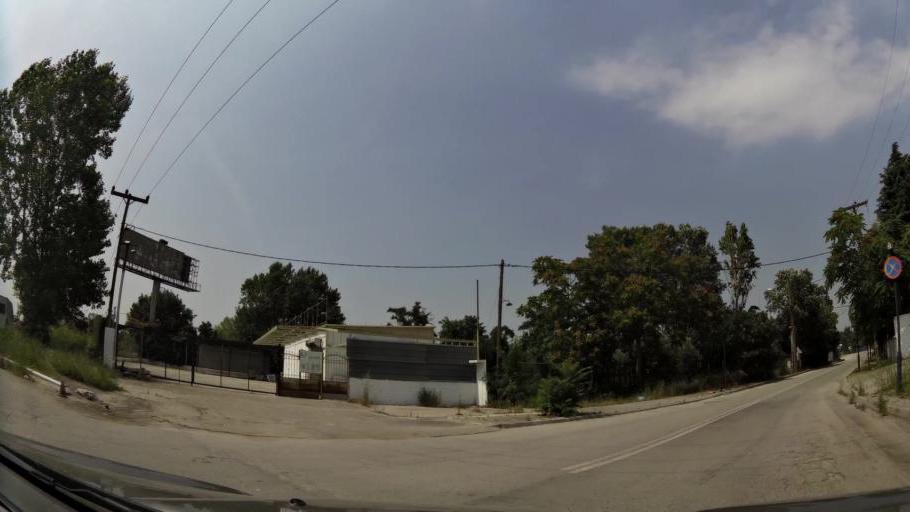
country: GR
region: Central Macedonia
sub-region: Nomos Thessalonikis
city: Menemeni
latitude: 40.6548
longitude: 22.8953
